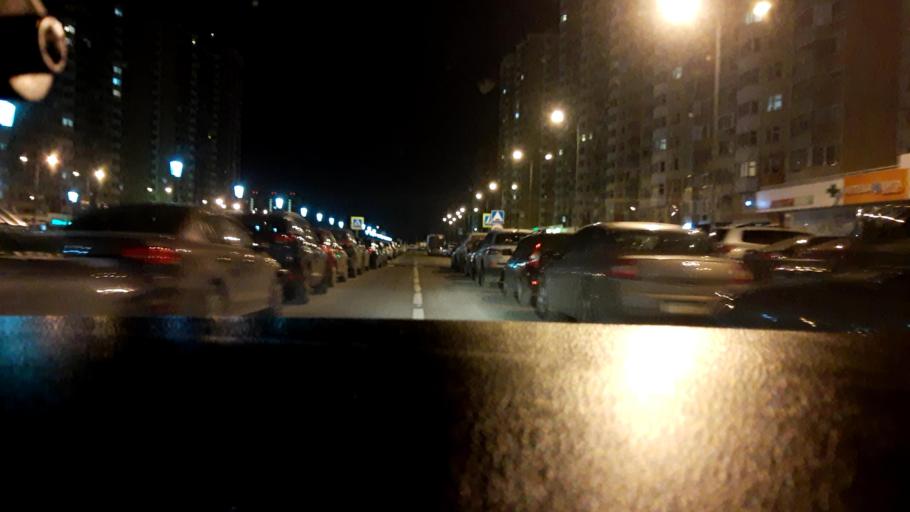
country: RU
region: Moskovskaya
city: Zheleznodorozhnyy
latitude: 55.7426
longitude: 38.0029
